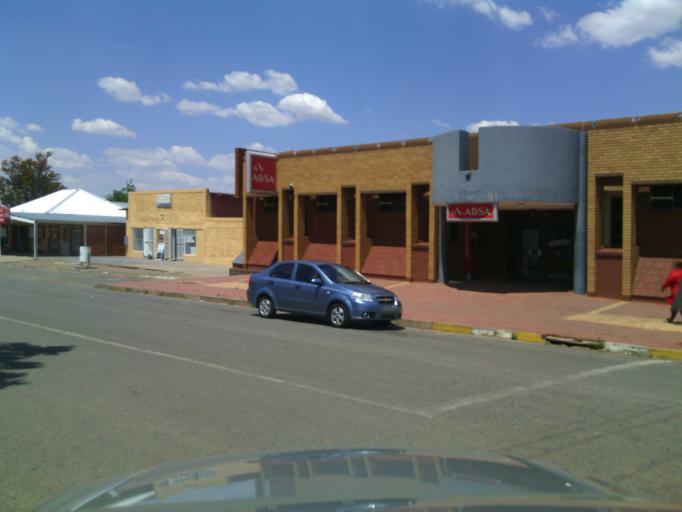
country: ZA
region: Orange Free State
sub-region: Xhariep District Municipality
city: Dewetsdorp
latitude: -29.5841
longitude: 26.6640
